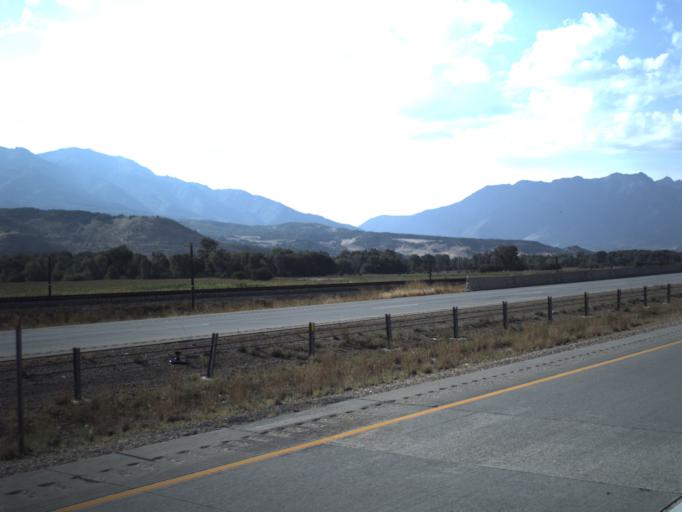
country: US
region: Utah
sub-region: Morgan County
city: Mountain Green
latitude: 41.0961
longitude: -111.7400
